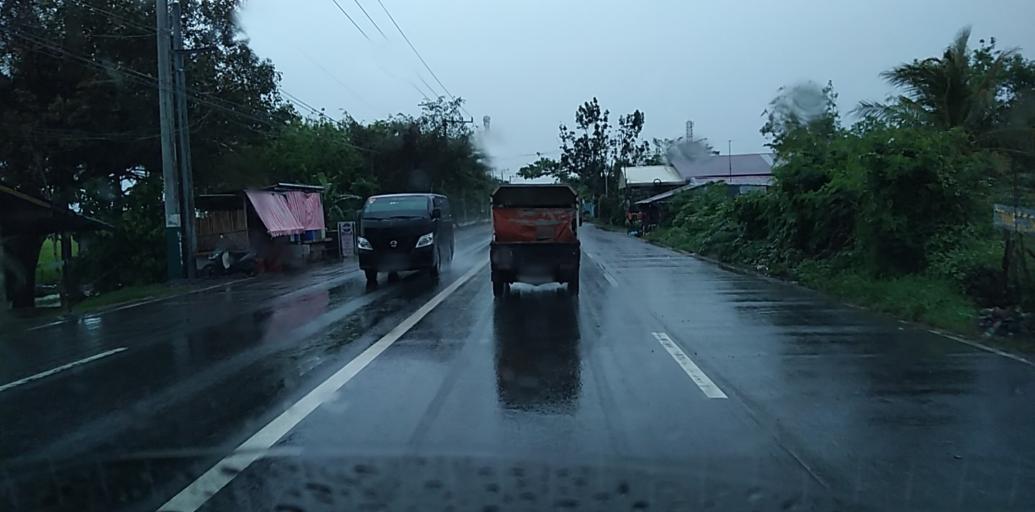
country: PH
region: Central Luzon
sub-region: Province of Bulacan
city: Bulualto
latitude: 15.2144
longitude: 120.9551
